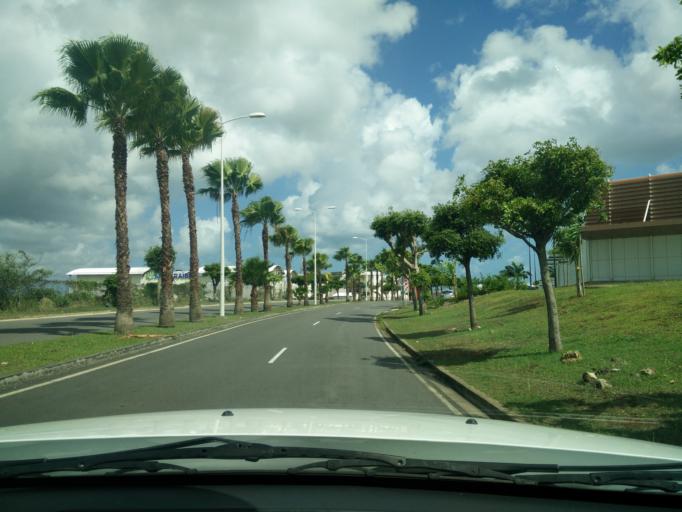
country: GP
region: Guadeloupe
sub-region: Guadeloupe
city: Les Abymes
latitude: 16.2664
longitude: -61.5169
